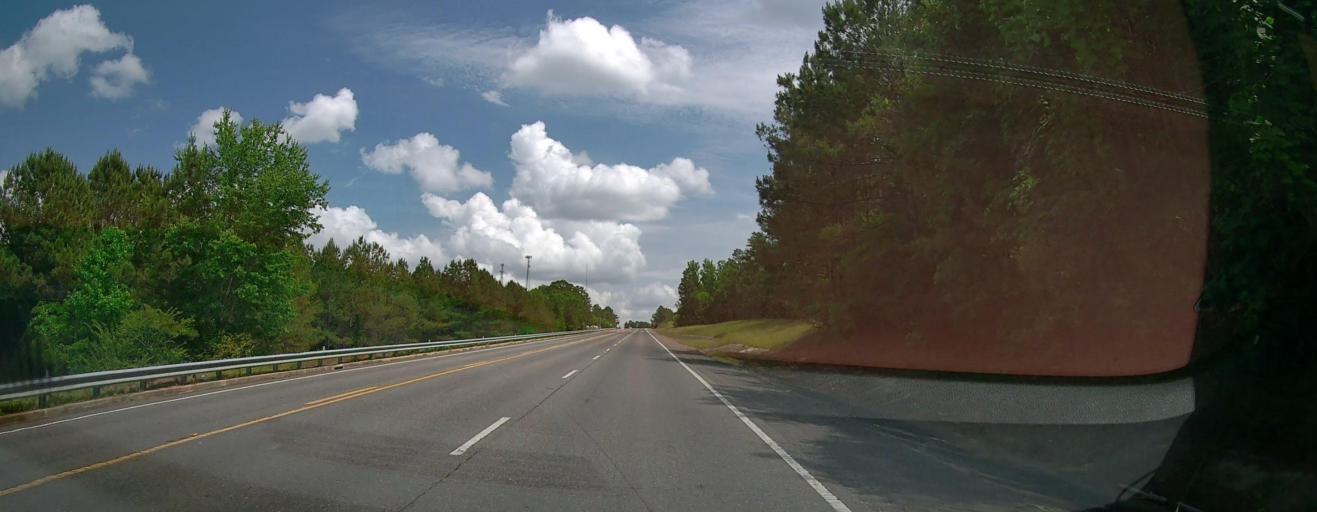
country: US
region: Alabama
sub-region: Marion County
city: Hamilton
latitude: 34.0876
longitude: -87.9809
